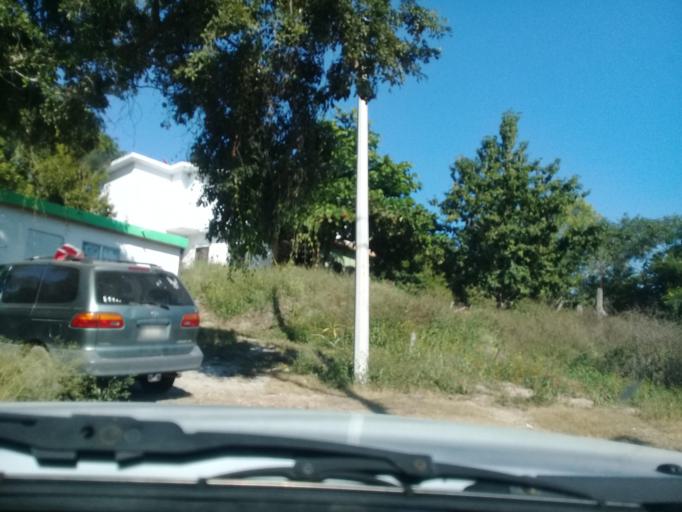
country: MX
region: Veracruz
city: Rinconada
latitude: 19.4009
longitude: -96.5610
